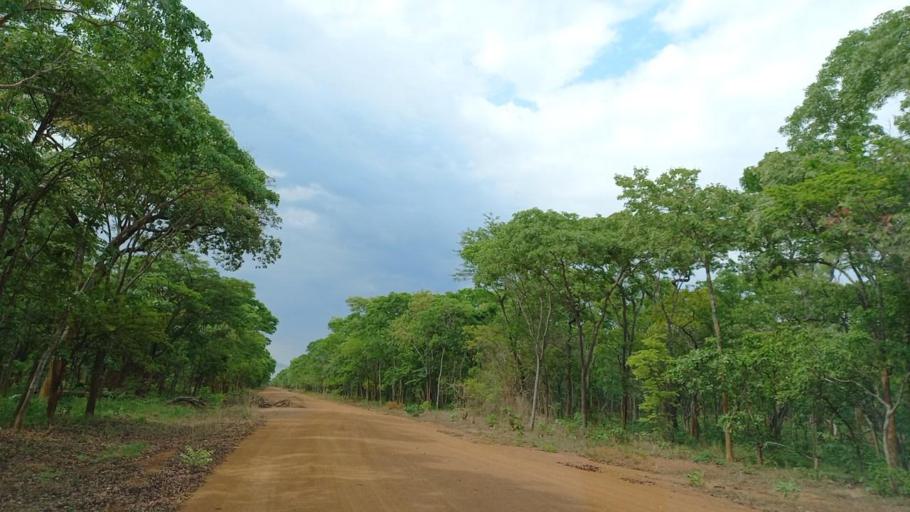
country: ZM
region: North-Western
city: Kalengwa
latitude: -13.3942
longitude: 25.0694
